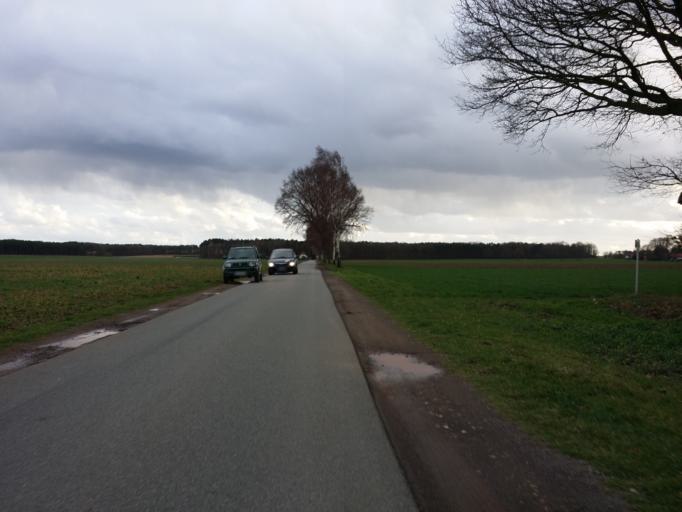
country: DE
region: Lower Saxony
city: Gross Ippener
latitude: 52.9795
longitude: 8.6335
